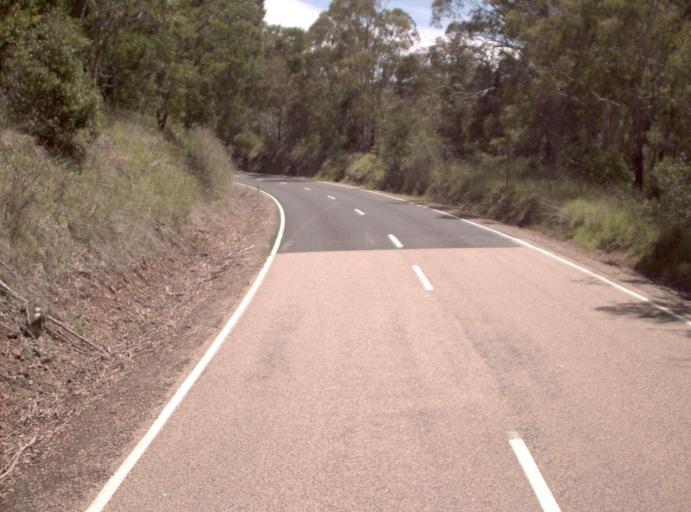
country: AU
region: Victoria
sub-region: East Gippsland
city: Lakes Entrance
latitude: -37.2438
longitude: 148.2559
